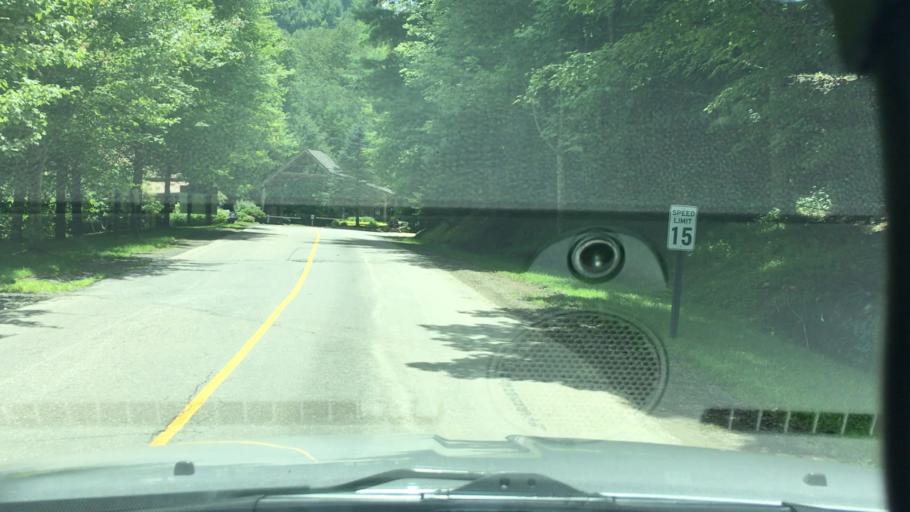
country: US
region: North Carolina
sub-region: Madison County
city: Mars Hill
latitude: 35.9543
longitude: -82.5167
